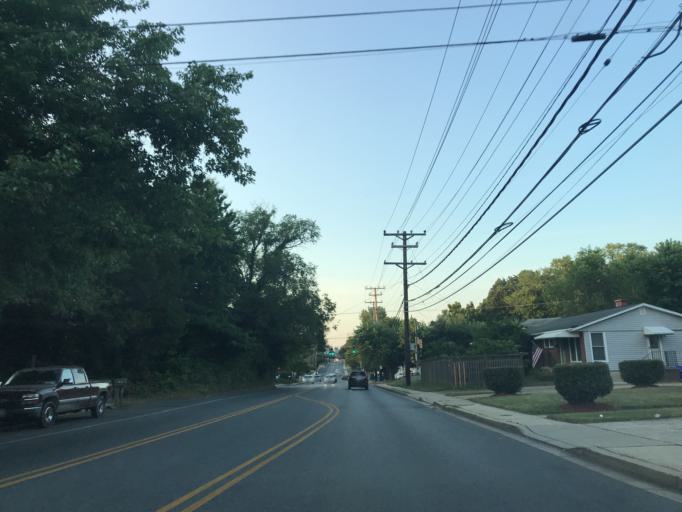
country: US
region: Maryland
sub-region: Anne Arundel County
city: Hillsmere Shores
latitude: 38.9590
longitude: -76.4913
